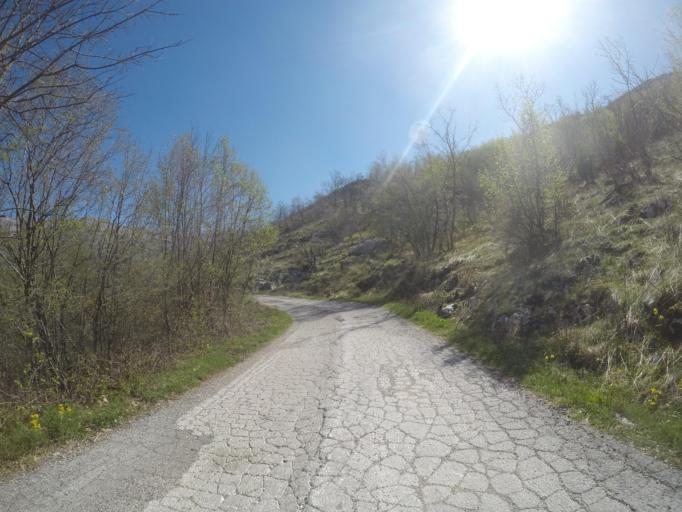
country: ME
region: Danilovgrad
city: Danilovgrad
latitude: 42.5371
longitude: 18.9918
